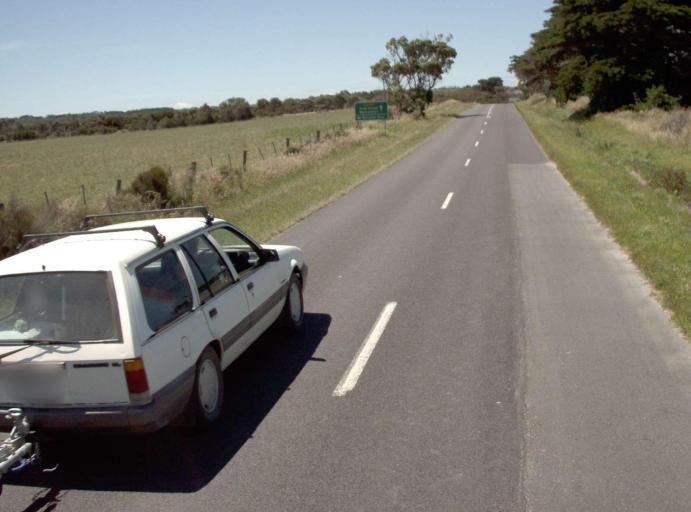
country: AU
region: Victoria
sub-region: Bass Coast
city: North Wonthaggi
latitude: -38.7981
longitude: 146.0864
